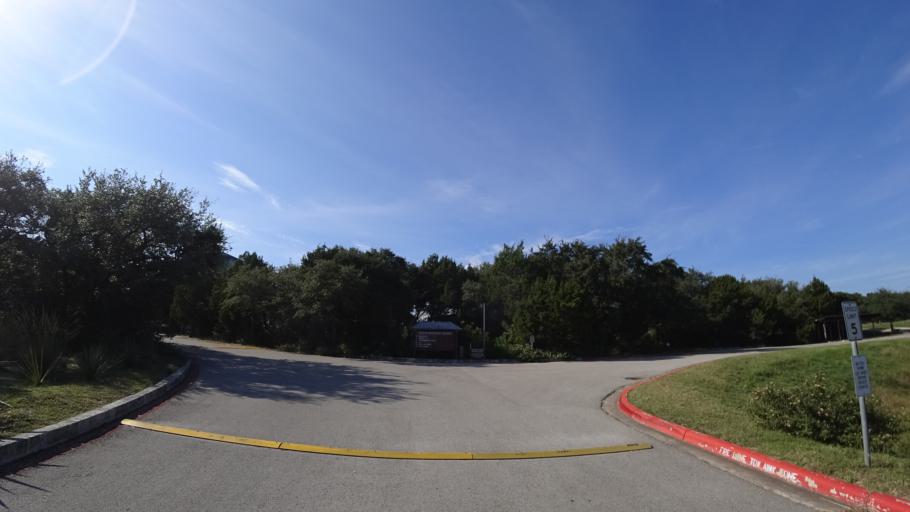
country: US
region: Texas
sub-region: Travis County
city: Barton Creek
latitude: 30.2318
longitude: -97.9119
